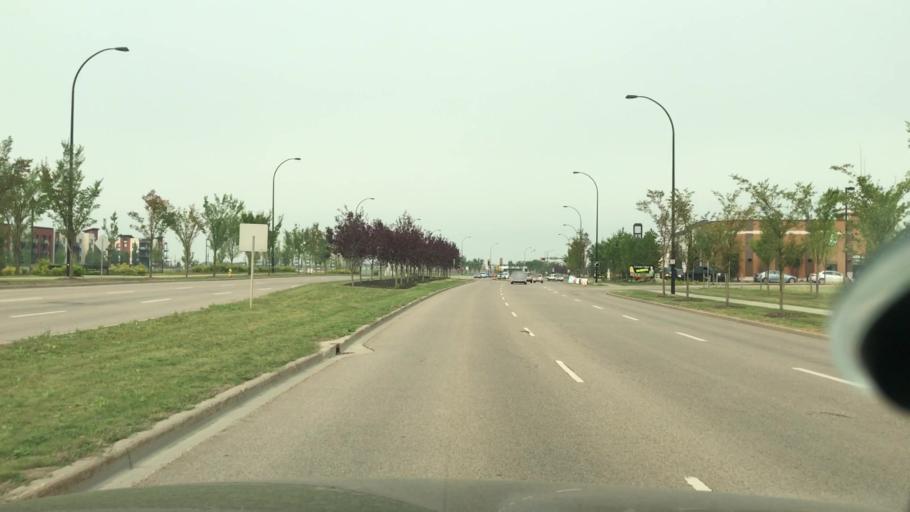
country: CA
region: Alberta
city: Devon
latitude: 53.4347
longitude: -113.6047
